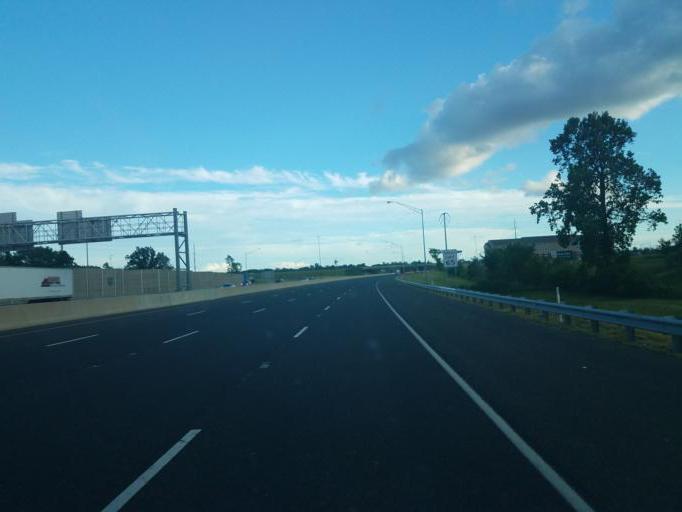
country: US
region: Indiana
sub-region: Allen County
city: Fort Wayne
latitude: 41.1733
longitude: -85.1035
